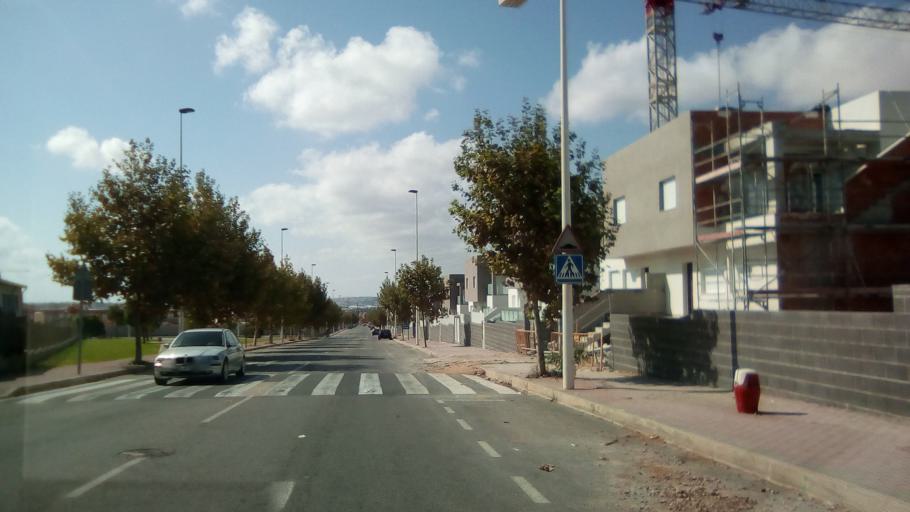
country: ES
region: Valencia
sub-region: Provincia de Alicante
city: Torrevieja
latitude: 38.0037
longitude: -0.6722
